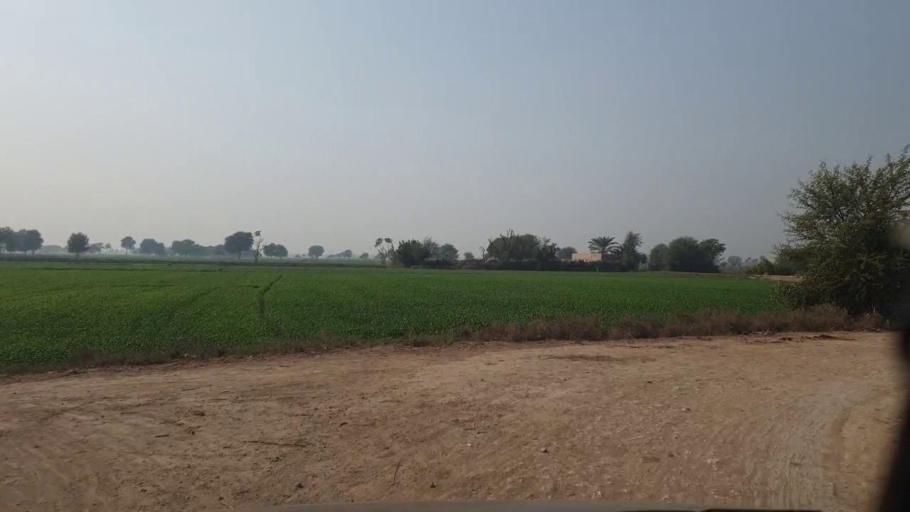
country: PK
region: Sindh
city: Shahdadpur
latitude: 26.0320
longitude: 68.5079
